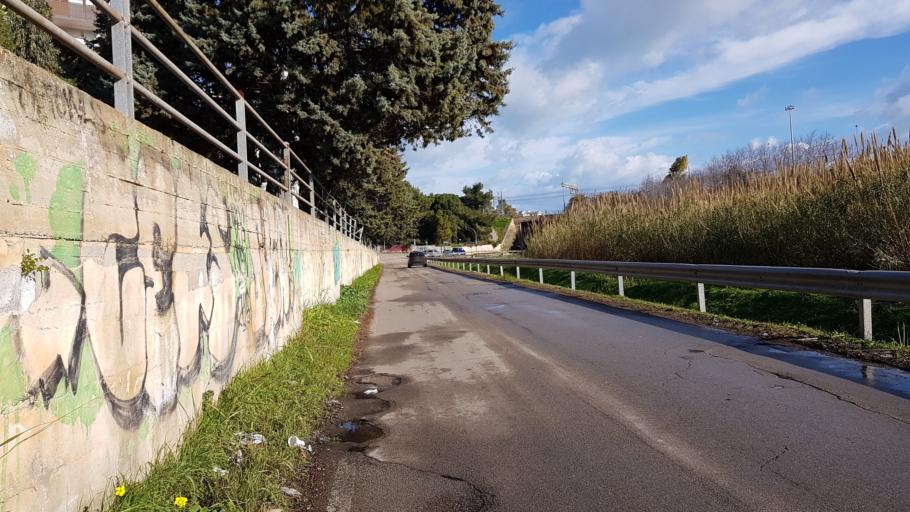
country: IT
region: Apulia
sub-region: Provincia di Brindisi
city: Brindisi
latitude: 40.6286
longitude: 17.9405
